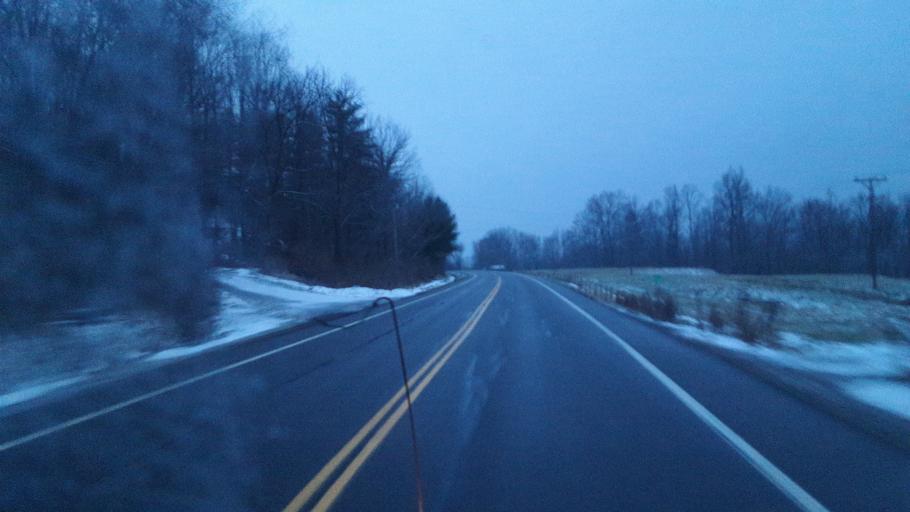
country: US
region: New York
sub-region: Allegany County
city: Belmont
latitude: 42.3132
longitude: -78.0968
